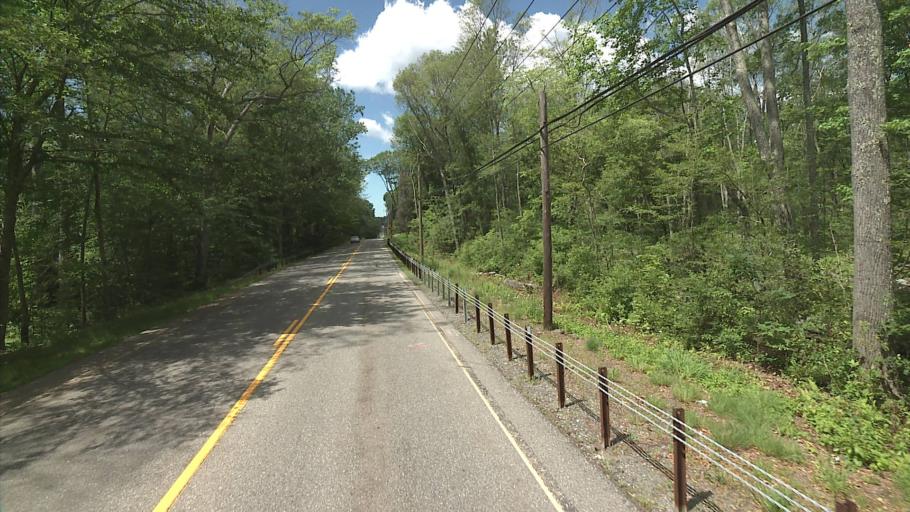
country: US
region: Connecticut
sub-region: New London County
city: Old Mystic
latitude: 41.4109
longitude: -71.9187
